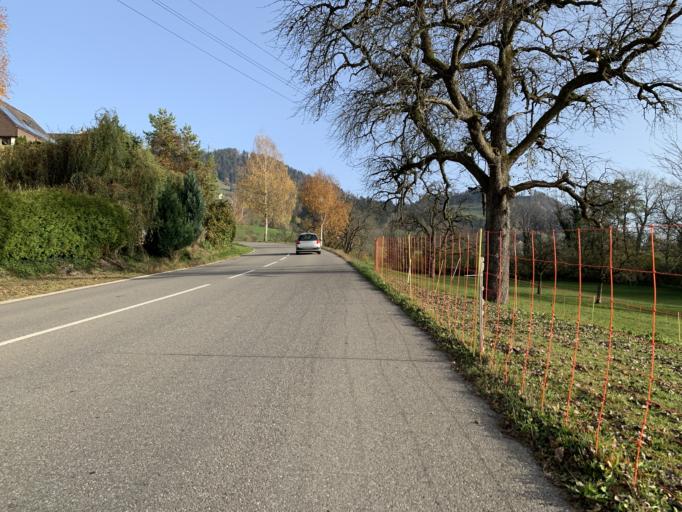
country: CH
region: Zurich
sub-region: Bezirk Hinwil
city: Hadlikon
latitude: 47.2969
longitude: 8.8615
